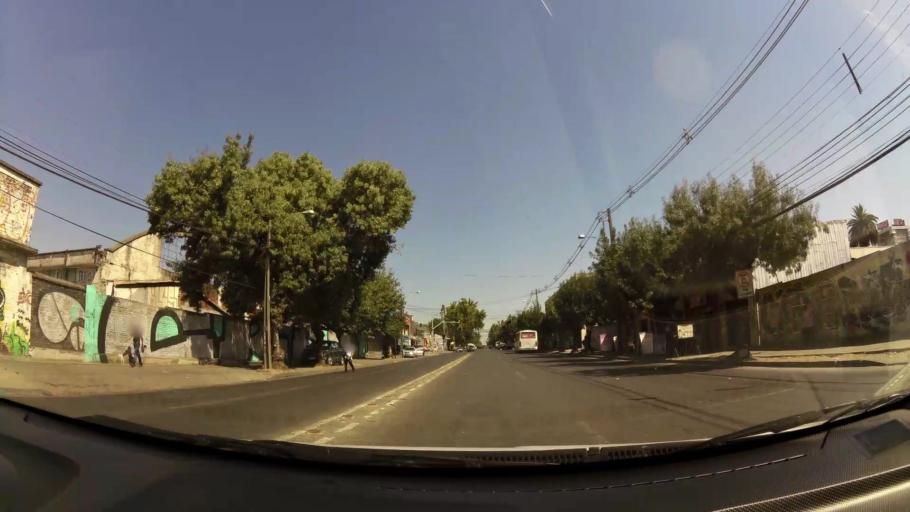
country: CL
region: Maule
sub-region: Provincia de Talca
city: Talca
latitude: -35.4265
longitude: -71.6501
